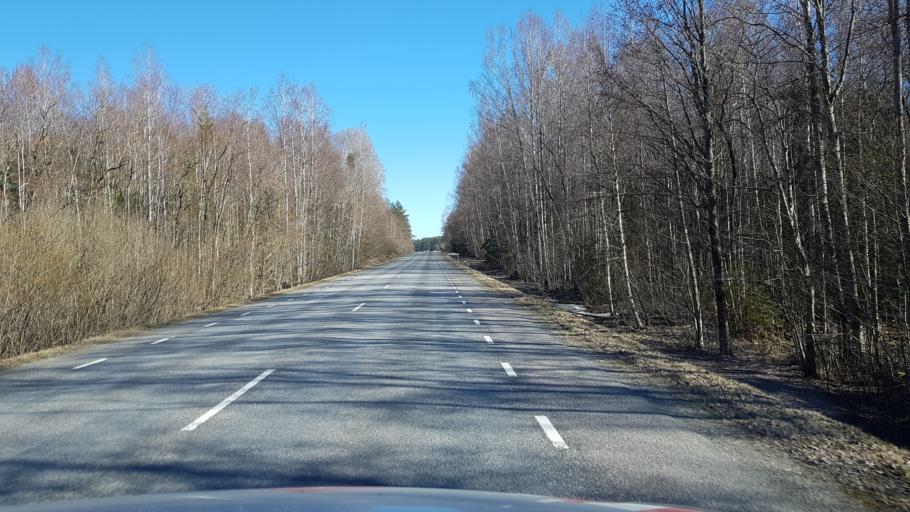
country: EE
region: Laeaene-Virumaa
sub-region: Viru-Nigula vald
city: Kunda
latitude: 59.3657
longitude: 26.6080
